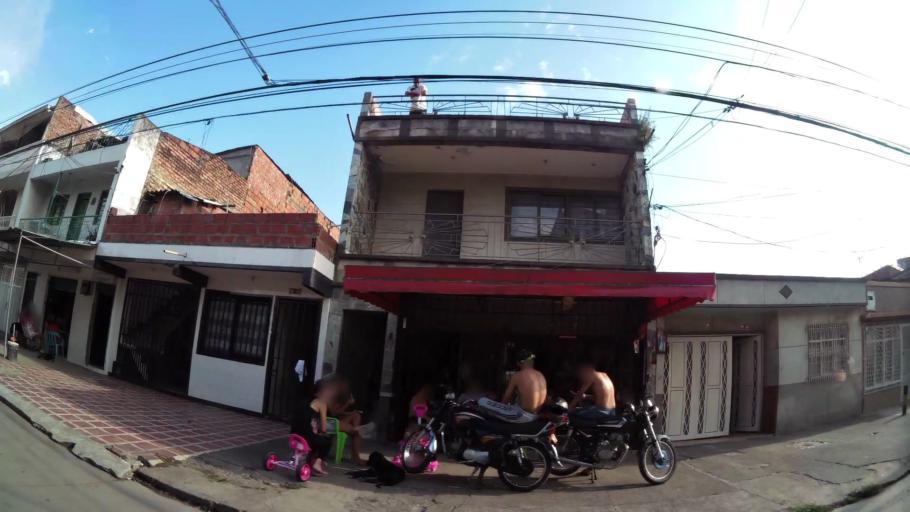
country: CO
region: Valle del Cauca
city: Cali
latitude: 3.4269
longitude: -76.5231
